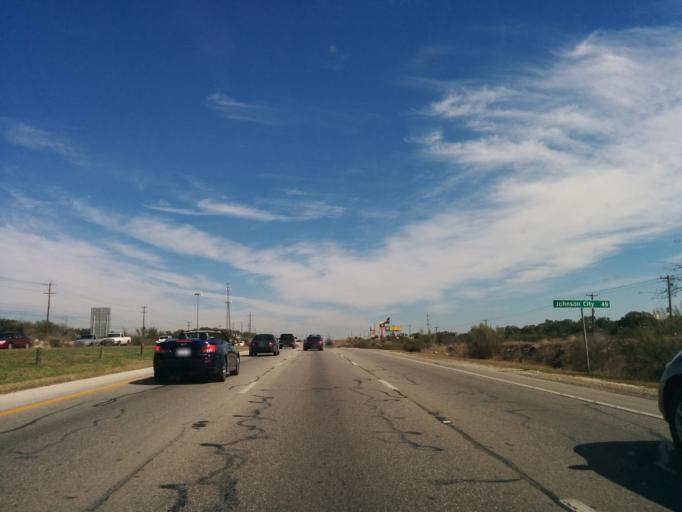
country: US
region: Texas
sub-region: Bexar County
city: Hollywood Park
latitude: 29.6246
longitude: -98.4631
